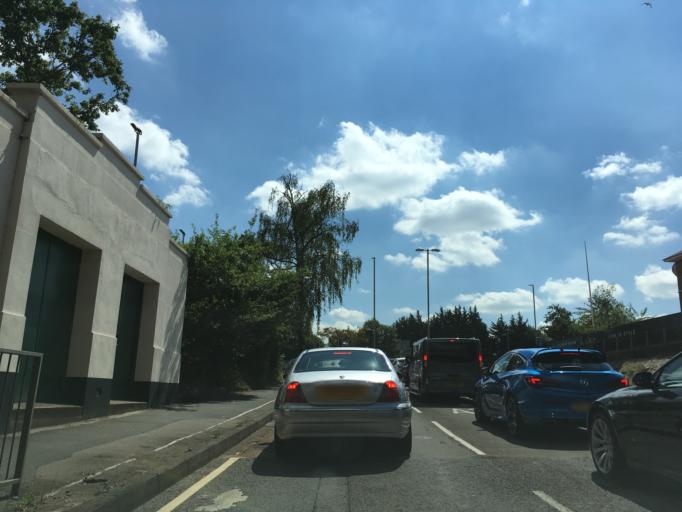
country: GB
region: England
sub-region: Gloucestershire
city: Barnwood
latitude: 51.8646
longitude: -2.2146
